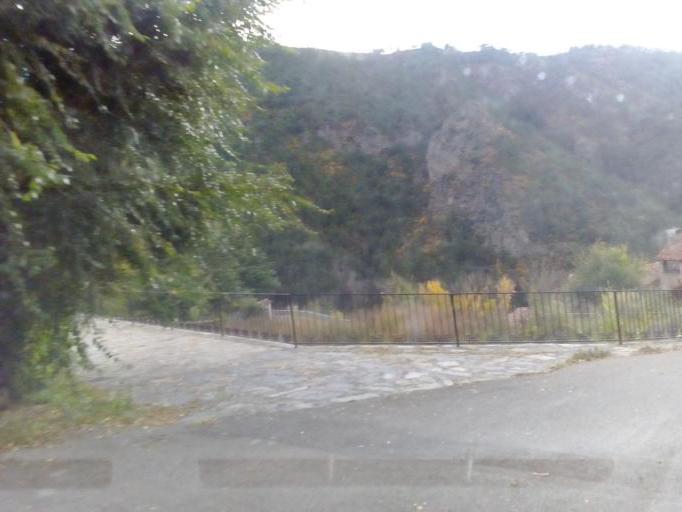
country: ES
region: Catalonia
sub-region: Provincia de Lleida
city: el Pont de Bar
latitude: 42.3503
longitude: 1.5846
